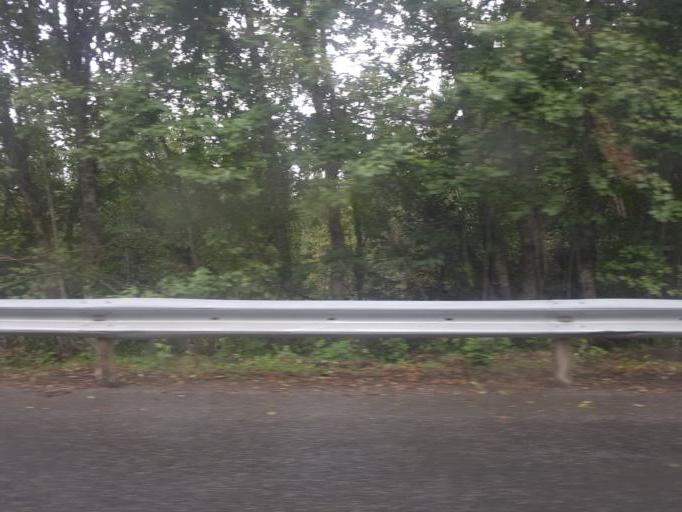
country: NO
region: Sor-Trondelag
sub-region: Trondheim
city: Trondheim
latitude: 63.4157
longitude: 10.2964
